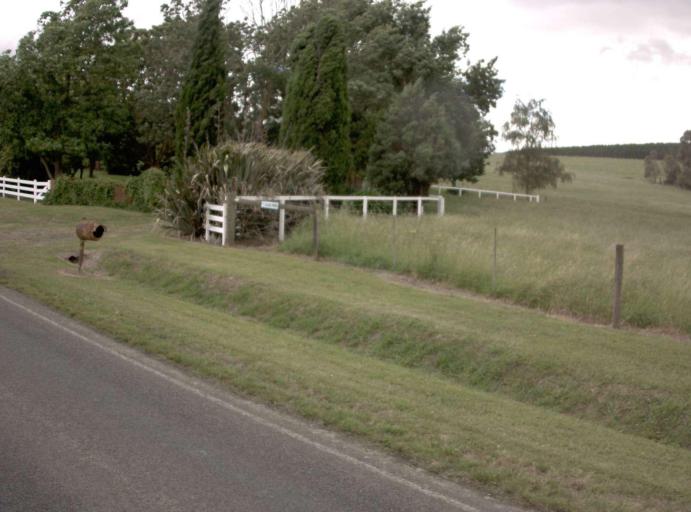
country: AU
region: Victoria
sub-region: Baw Baw
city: Warragul
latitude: -38.1406
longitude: 145.9862
